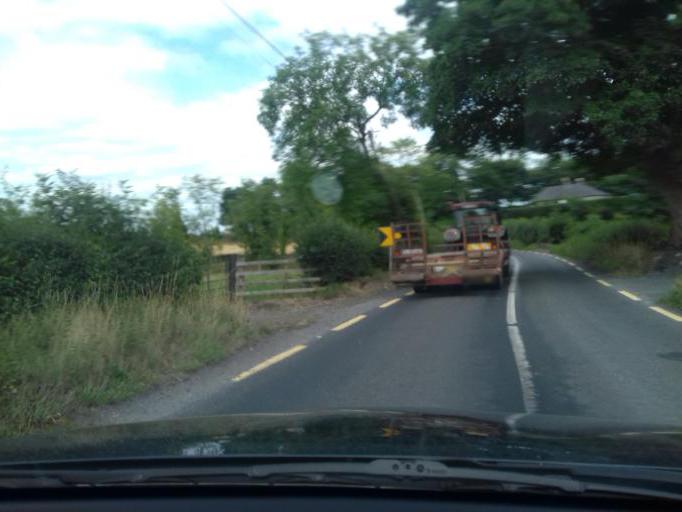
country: IE
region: Leinster
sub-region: County Carlow
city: Tullow
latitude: 52.8235
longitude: -6.7243
